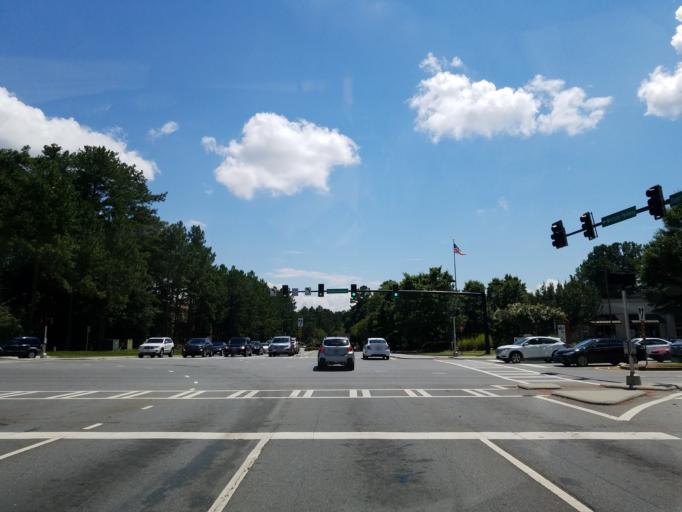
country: US
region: Georgia
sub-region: Fulton County
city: Alpharetta
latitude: 34.0880
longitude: -84.2694
